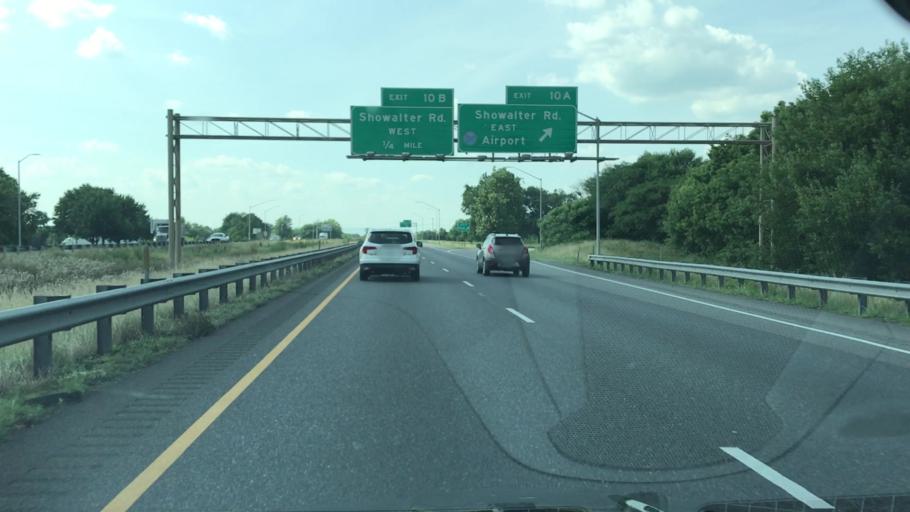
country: US
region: Maryland
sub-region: Washington County
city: Maugansville
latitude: 39.6972
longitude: -77.7367
